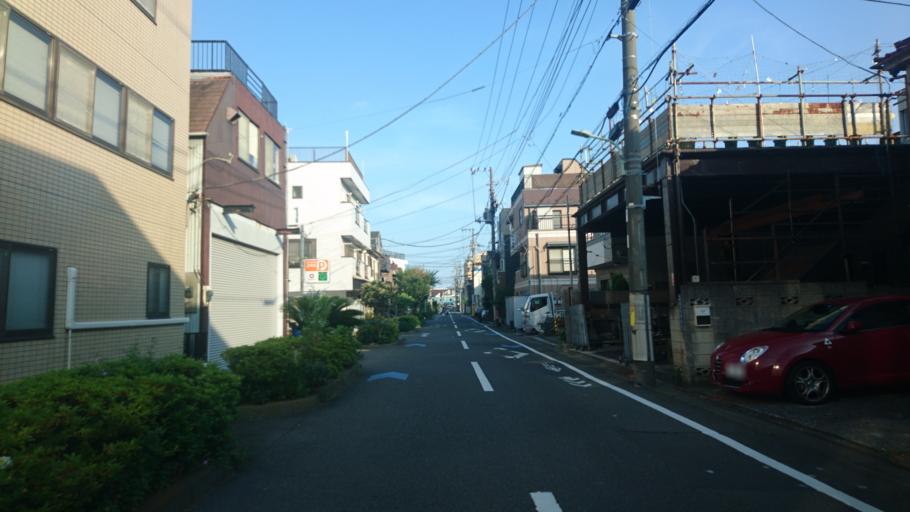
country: JP
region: Kanagawa
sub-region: Kawasaki-shi
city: Kawasaki
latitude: 35.5774
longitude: 139.7201
